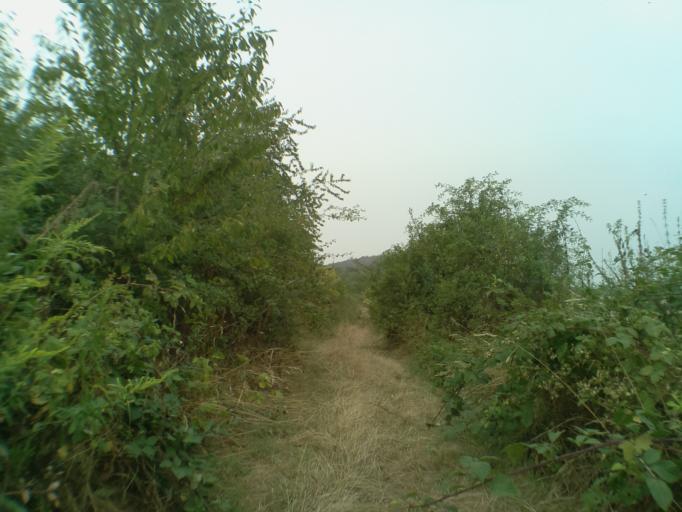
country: PL
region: Lower Silesian Voivodeship
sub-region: Powiat swidnicki
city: Strzegom
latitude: 50.9939
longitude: 16.2902
